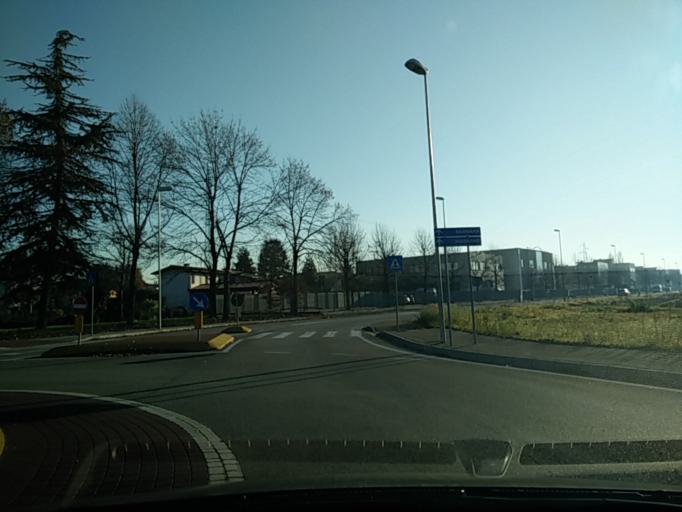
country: IT
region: Veneto
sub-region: Provincia di Padova
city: Noventa
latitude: 45.3991
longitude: 11.9366
